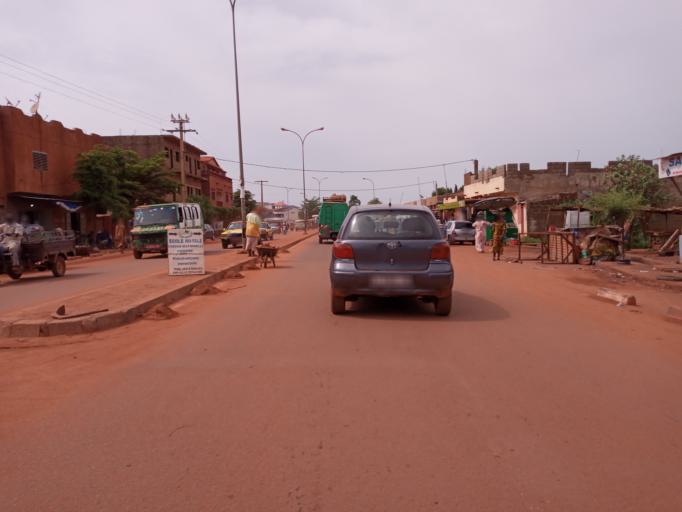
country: ML
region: Bamako
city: Bamako
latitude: 12.5502
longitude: -7.9991
